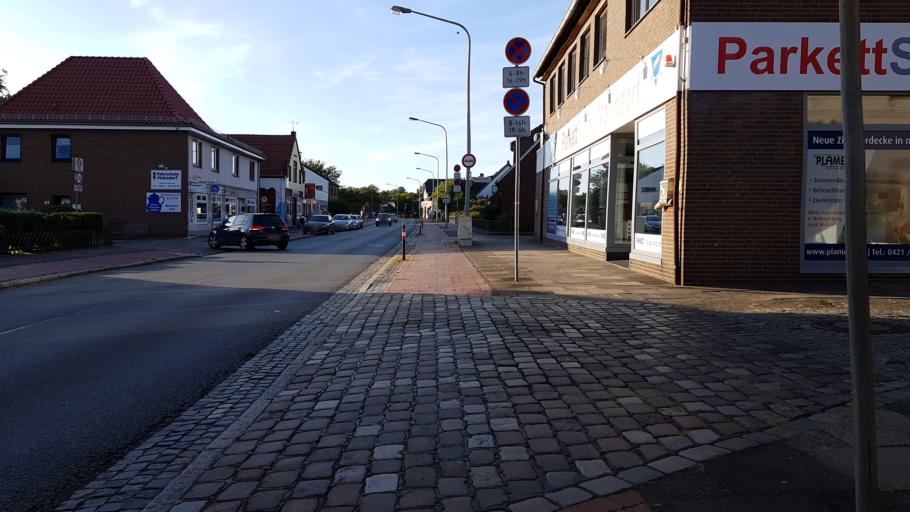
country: DE
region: Lower Saxony
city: Riede
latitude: 53.0368
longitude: 8.9467
